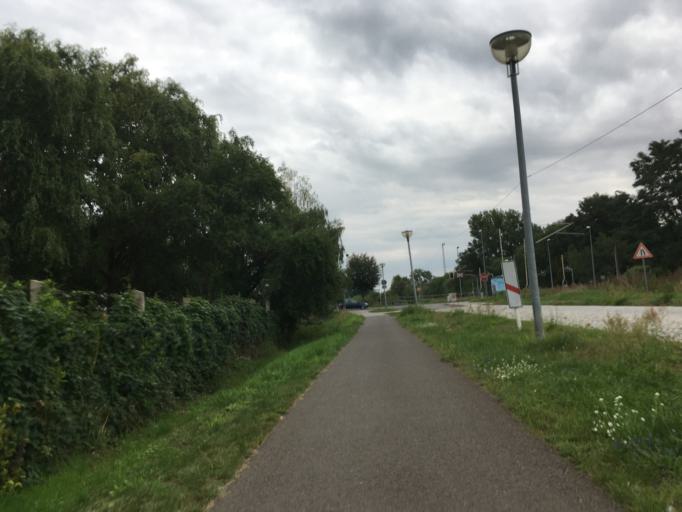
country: DE
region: Brandenburg
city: Schwedt (Oder)
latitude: 53.0665
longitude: 14.2784
